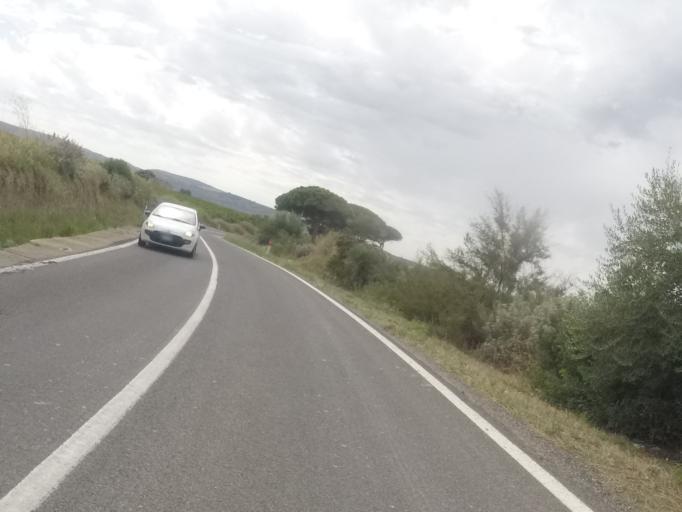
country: IT
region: Sardinia
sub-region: Provincia di Sassari
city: Sorso
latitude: 40.8401
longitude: 8.6032
